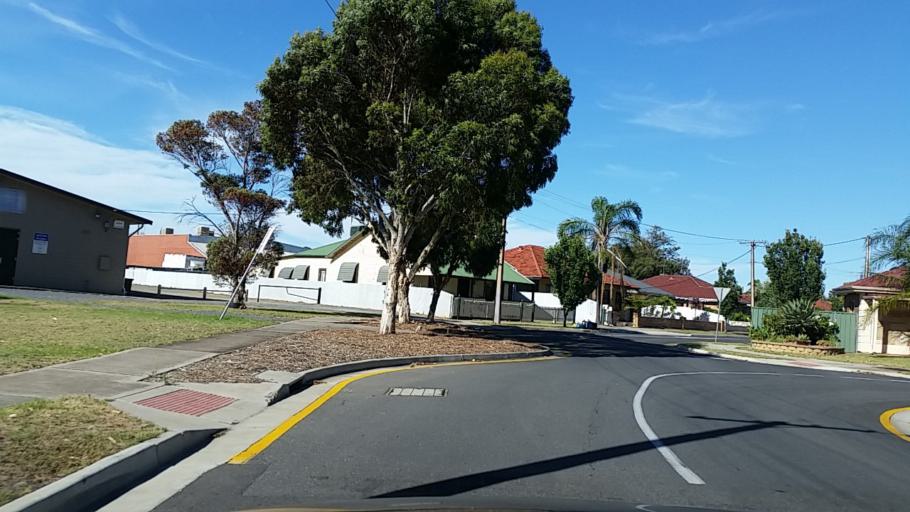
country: AU
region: South Australia
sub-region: Charles Sturt
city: Royal Park
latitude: -34.8700
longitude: 138.5056
